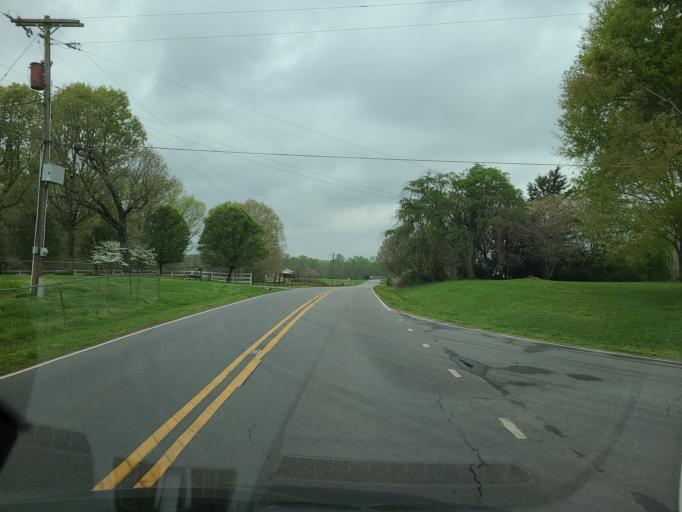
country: US
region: North Carolina
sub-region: Lincoln County
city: Lincolnton
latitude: 35.4608
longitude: -81.3260
